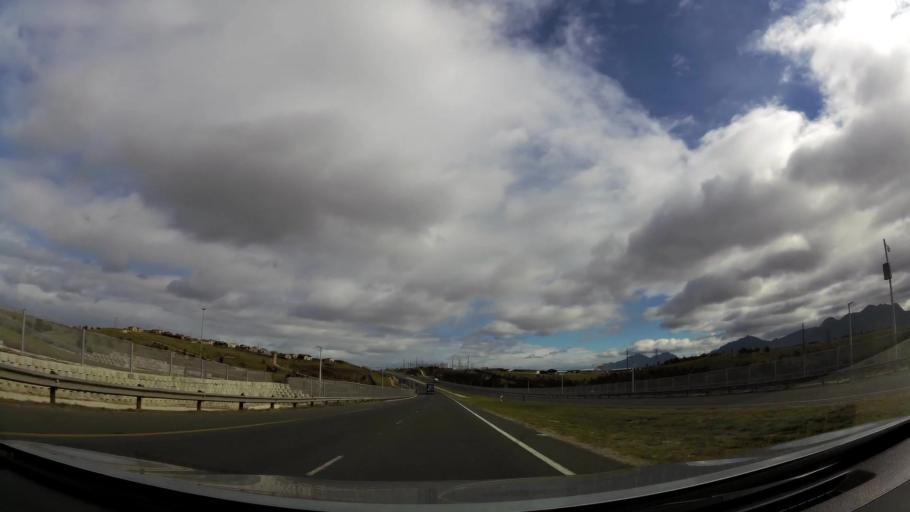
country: ZA
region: Western Cape
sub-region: Eden District Municipality
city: George
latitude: -33.9957
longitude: 22.4639
